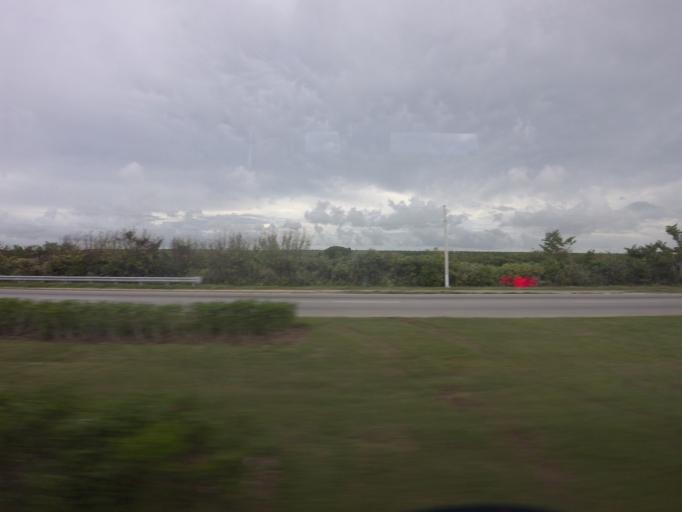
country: CU
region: Matanzas
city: Varadero
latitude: 23.1071
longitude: -81.3892
